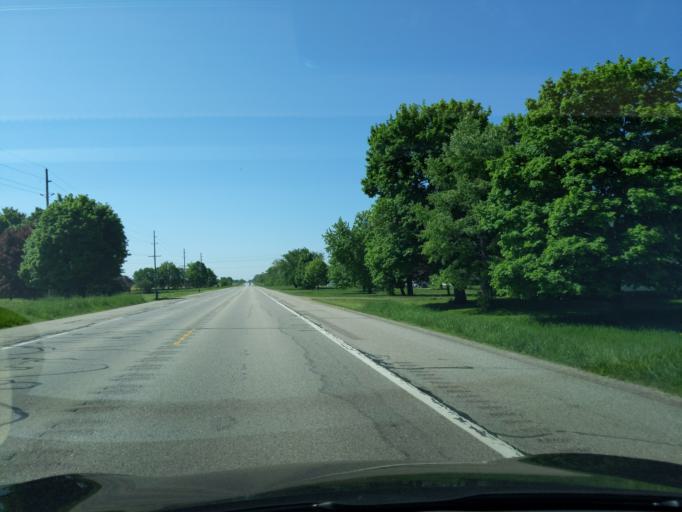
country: US
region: Michigan
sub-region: Ingham County
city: Webberville
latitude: 42.5648
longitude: -84.1920
